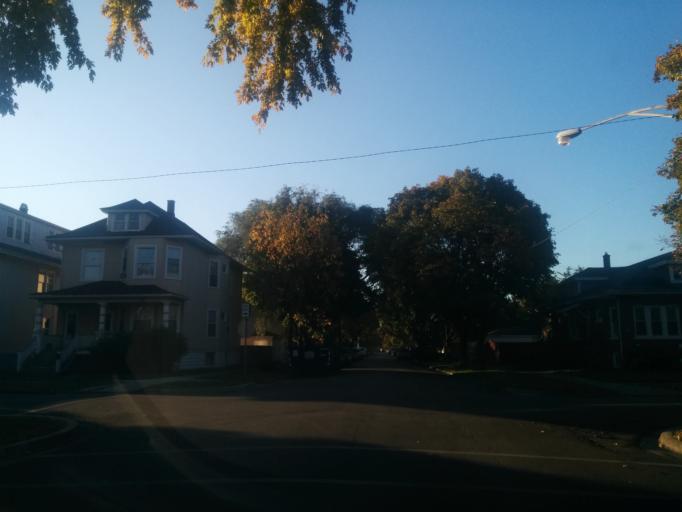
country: US
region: Illinois
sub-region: Cook County
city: Elmwood Park
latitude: 41.9381
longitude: -87.7517
